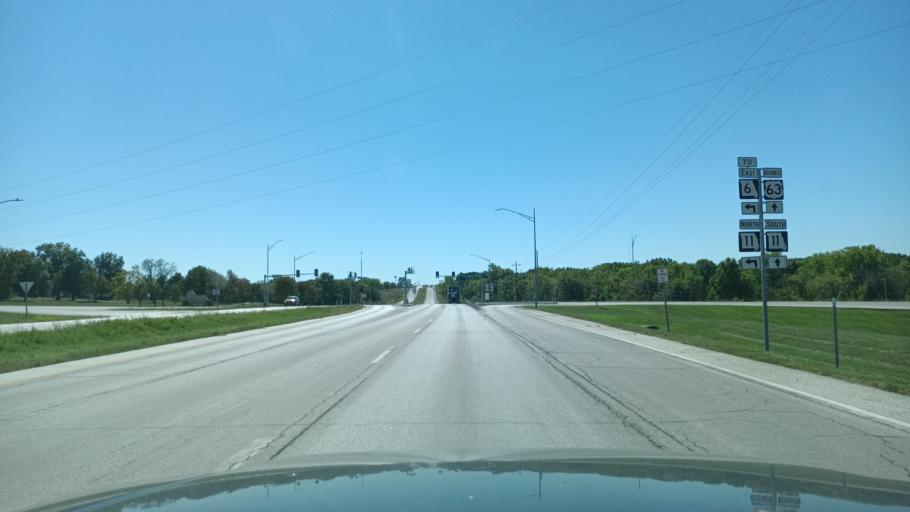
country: US
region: Missouri
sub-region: Adair County
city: Kirksville
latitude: 40.1694
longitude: -92.5722
